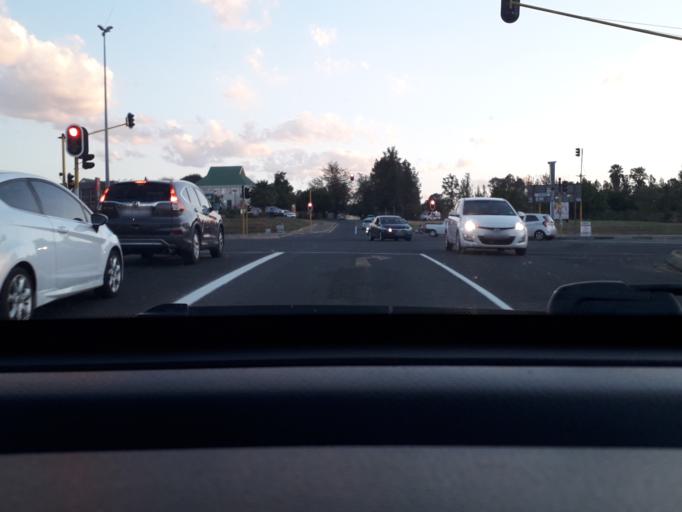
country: ZA
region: Gauteng
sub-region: City of Johannesburg Metropolitan Municipality
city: Diepsloot
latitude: -26.0252
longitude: 28.0211
